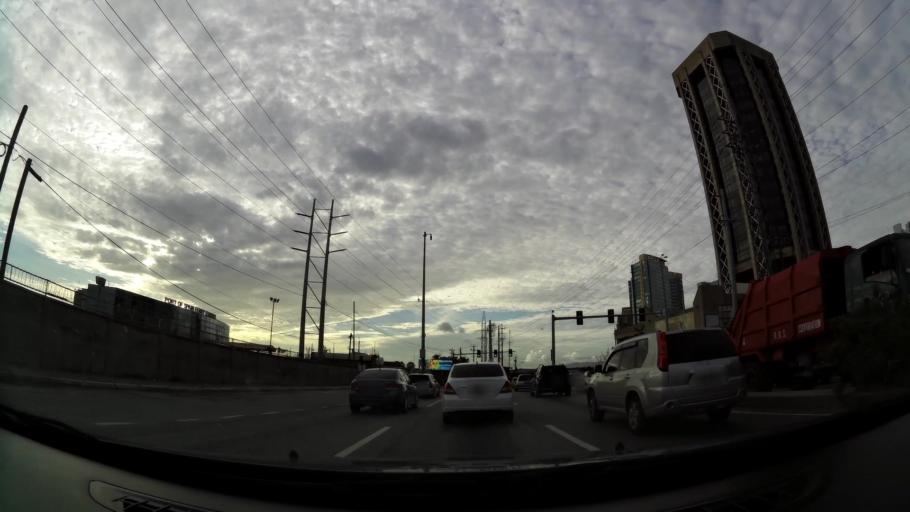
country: TT
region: San Juan/Laventille
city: Laventille
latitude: 10.6478
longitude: -61.5115
